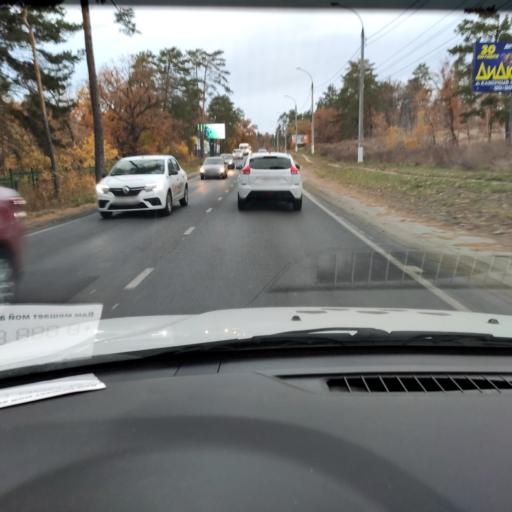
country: RU
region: Samara
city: Tol'yatti
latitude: 53.4835
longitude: 49.3177
